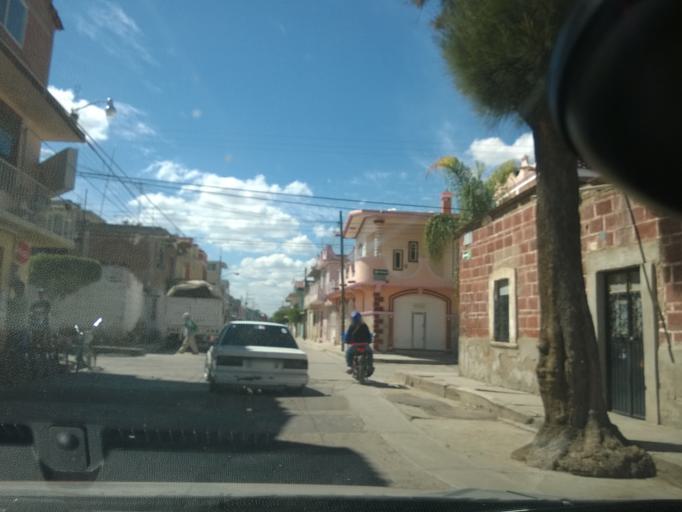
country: MX
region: Guanajuato
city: Romita
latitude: 20.8737
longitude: -101.5192
